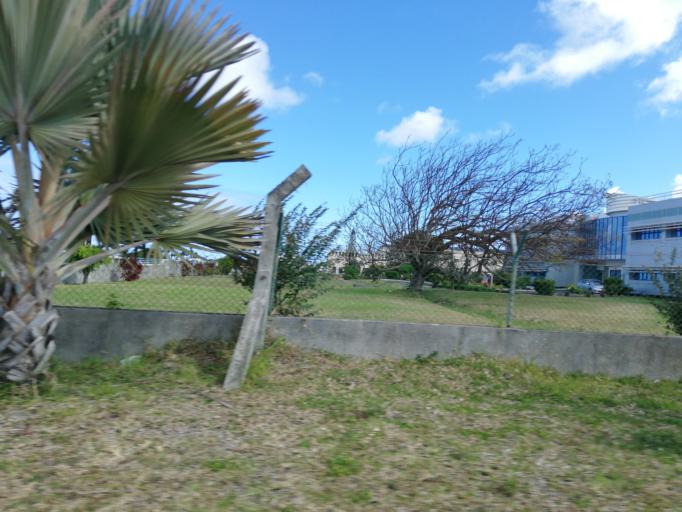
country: MU
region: Grand Port
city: Plaine Magnien
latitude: -20.4355
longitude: 57.6762
